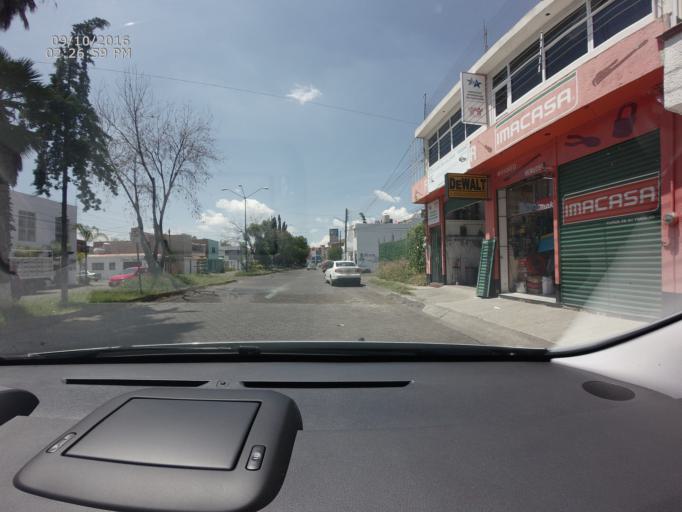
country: MX
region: Michoacan
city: Morelia
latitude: 19.6840
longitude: -101.2173
